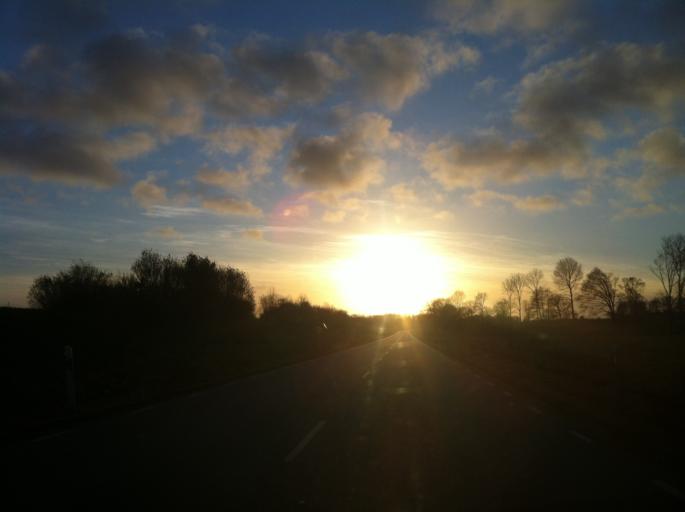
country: SE
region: Skane
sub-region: Hoors Kommun
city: Hoeoer
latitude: 55.9459
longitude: 13.5392
